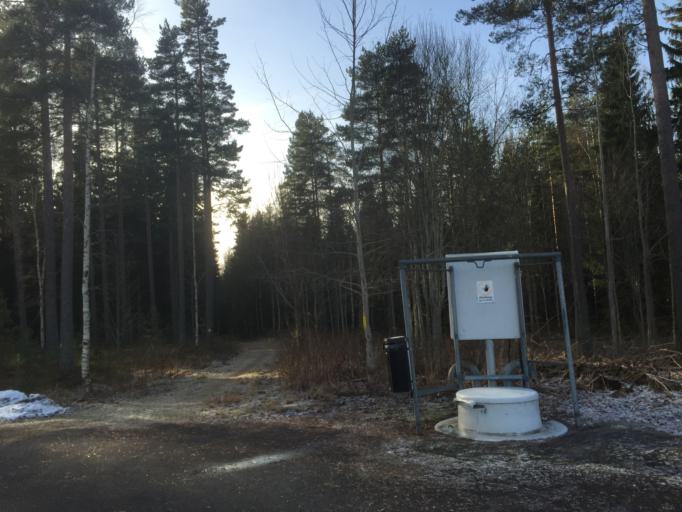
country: SE
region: Joenkoeping
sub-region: Aneby Kommun
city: Aneby
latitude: 57.8457
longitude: 14.7949
